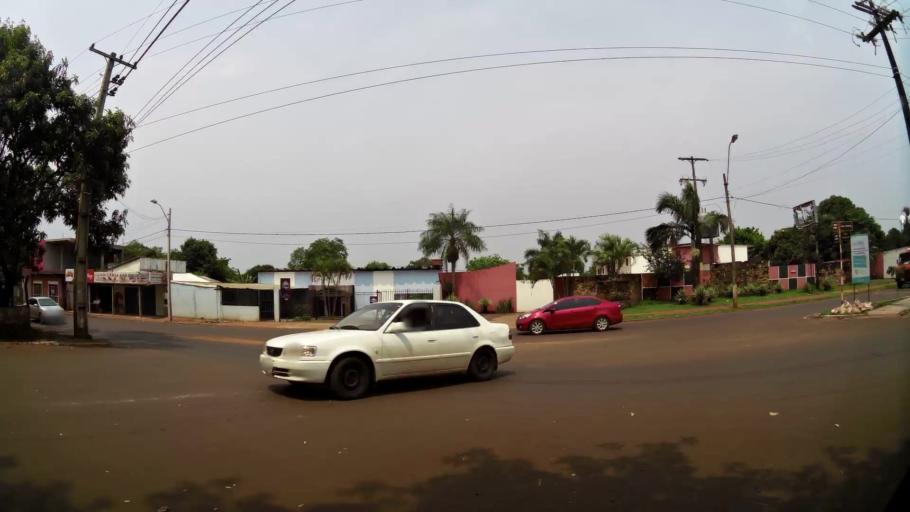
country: PY
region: Alto Parana
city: Presidente Franco
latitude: -25.5559
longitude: -54.6258
